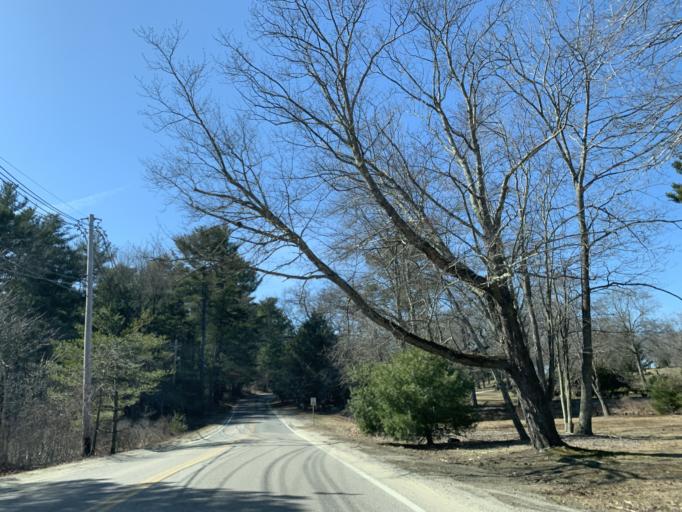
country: US
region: Massachusetts
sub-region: Norfolk County
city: Sharon
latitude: 42.1429
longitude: -71.1726
